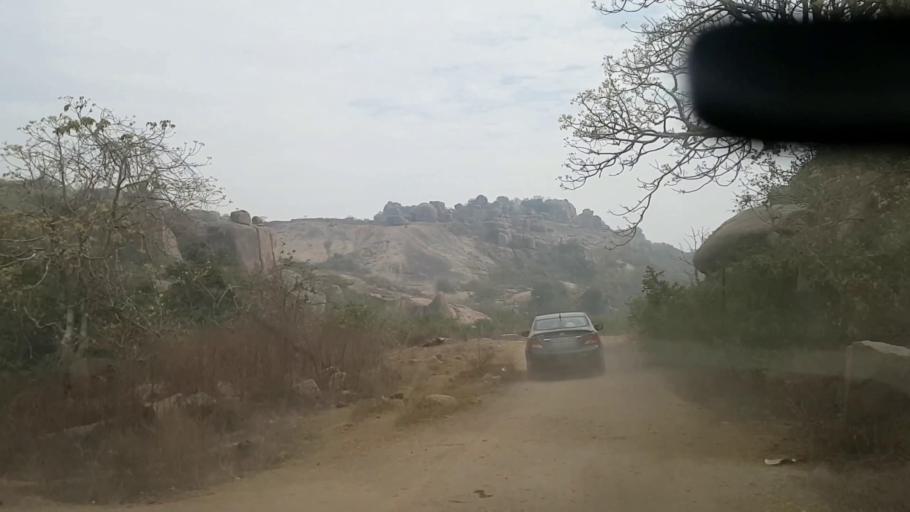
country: IN
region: Telangana
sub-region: Rangareddi
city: Lal Bahadur Nagar
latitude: 17.1802
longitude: 78.7992
